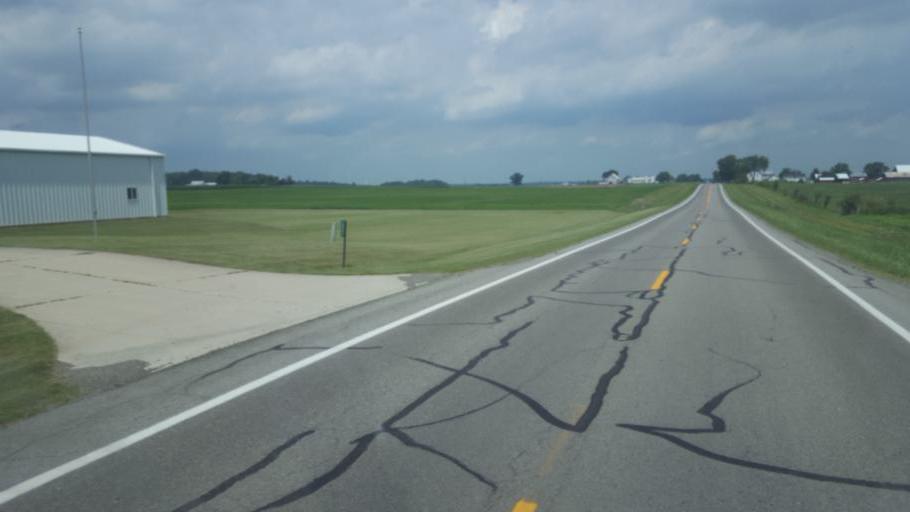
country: US
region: Ohio
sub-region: Hardin County
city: Kenton
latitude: 40.5906
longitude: -83.5929
